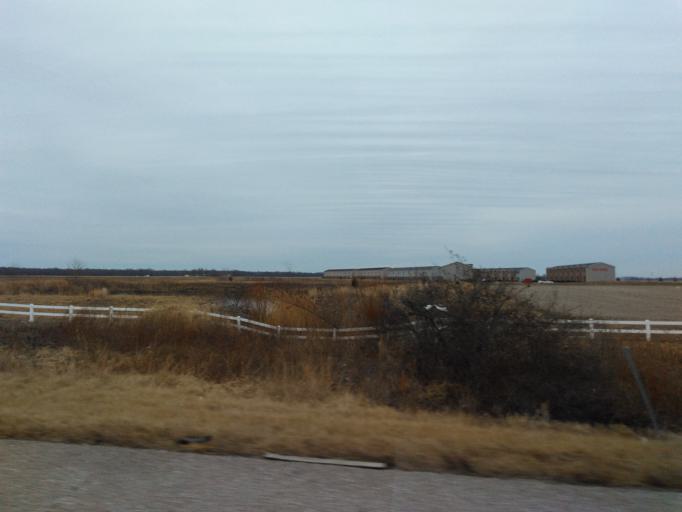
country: US
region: Illinois
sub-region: Saint Clair County
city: Scott Air Force Base
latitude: 38.5542
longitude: -89.8157
